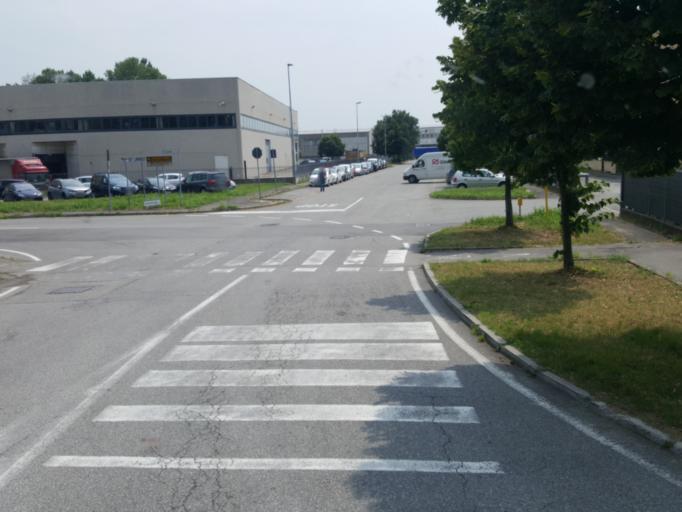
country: IT
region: Lombardy
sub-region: Citta metropolitana di Milano
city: Truccazzano
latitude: 45.4804
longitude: 9.4516
